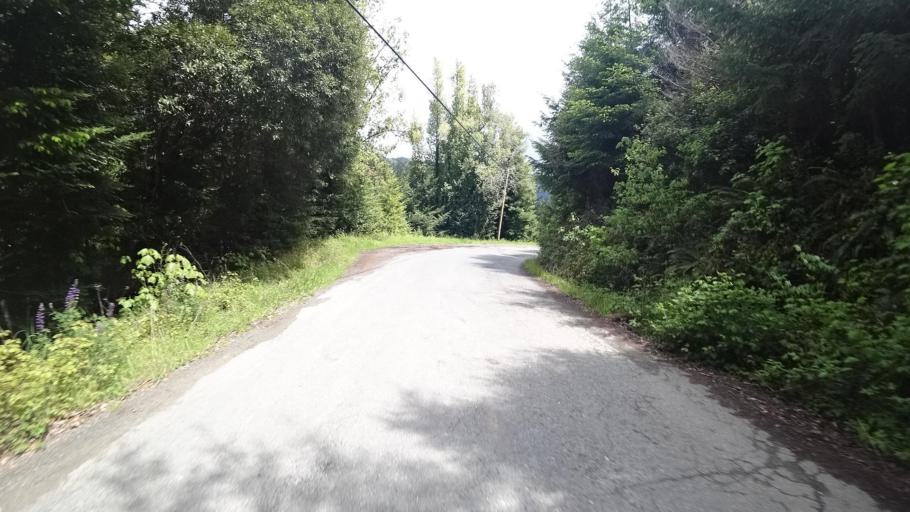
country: US
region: California
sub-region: Humboldt County
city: Blue Lake
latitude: 40.8014
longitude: -123.8785
